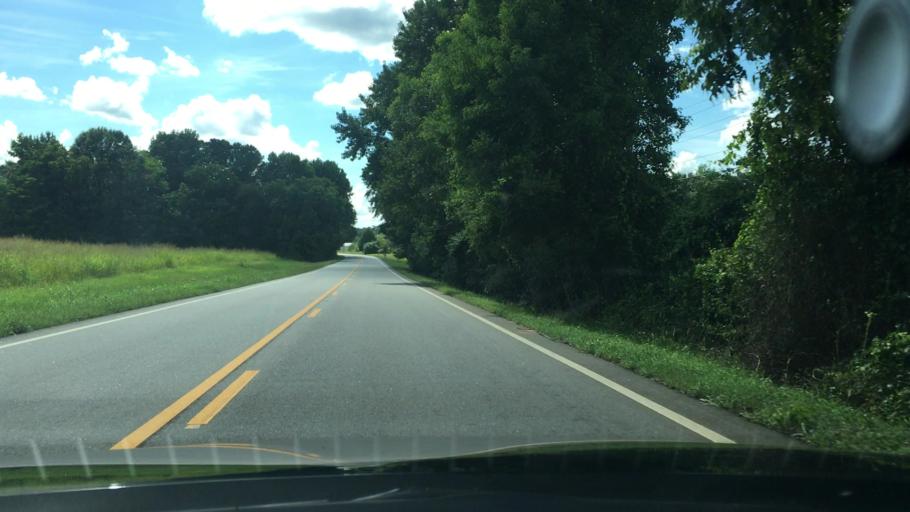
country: US
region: Georgia
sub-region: Butts County
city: Indian Springs
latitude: 33.2886
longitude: -83.9139
